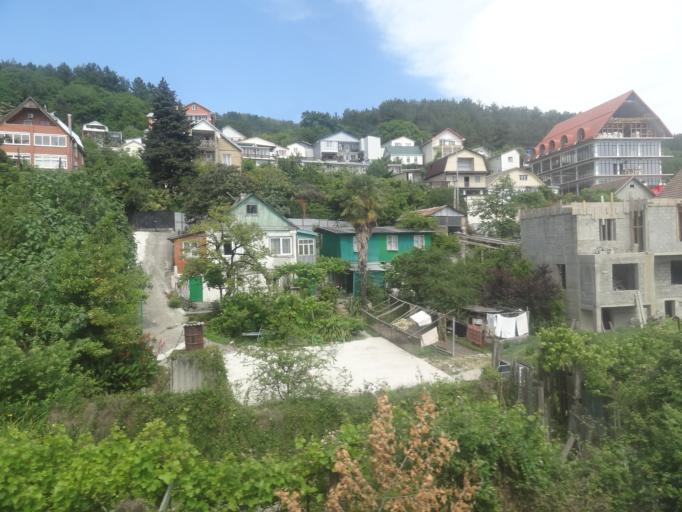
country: RU
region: Krasnodarskiy
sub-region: Sochi City
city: Lazarevskoye
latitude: 43.9389
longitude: 39.2990
